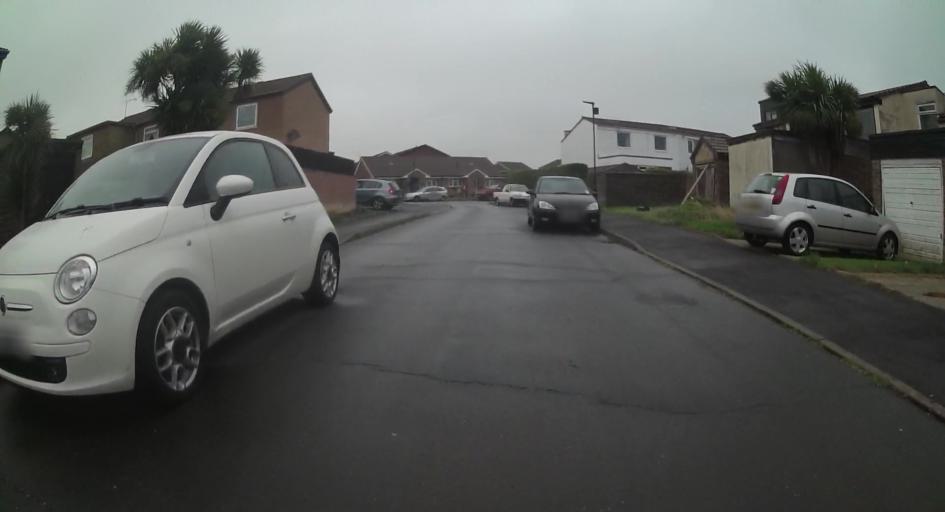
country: GB
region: England
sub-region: Isle of Wight
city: Newchurch
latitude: 50.6519
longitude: -1.2014
